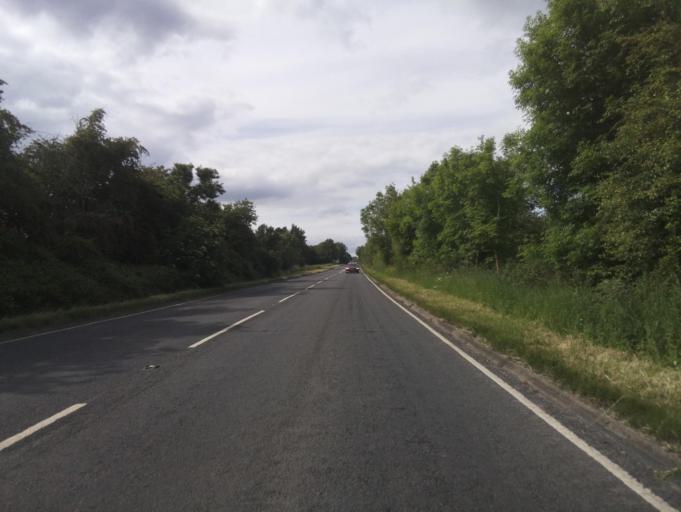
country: GB
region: England
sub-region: Worcestershire
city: Pershore
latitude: 52.1431
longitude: -2.1383
